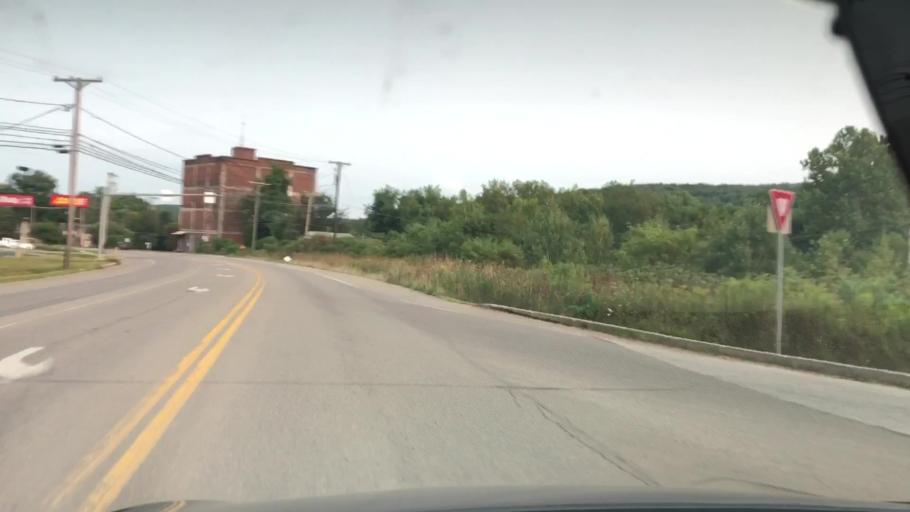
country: US
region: Pennsylvania
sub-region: Crawford County
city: Titusville
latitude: 41.6332
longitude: -79.6953
